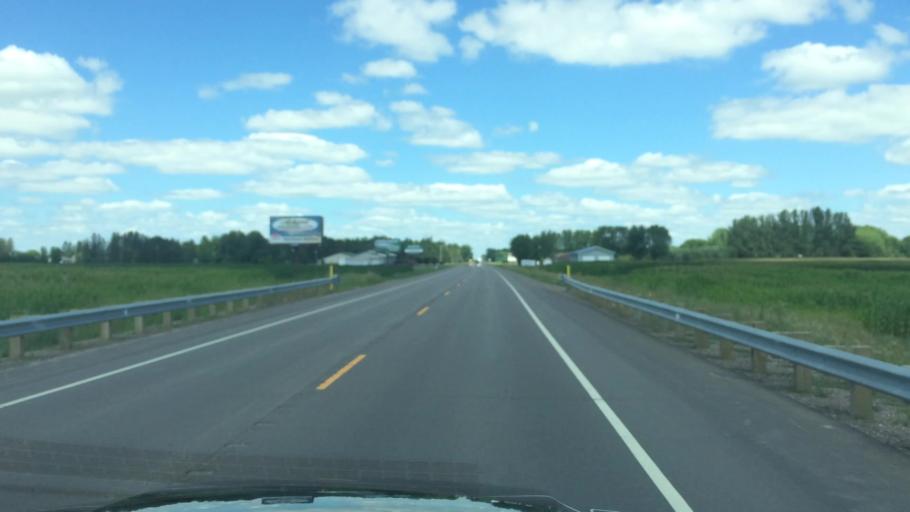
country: US
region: Wisconsin
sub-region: Clark County
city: Abbotsford
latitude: 45.0135
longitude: -90.3153
